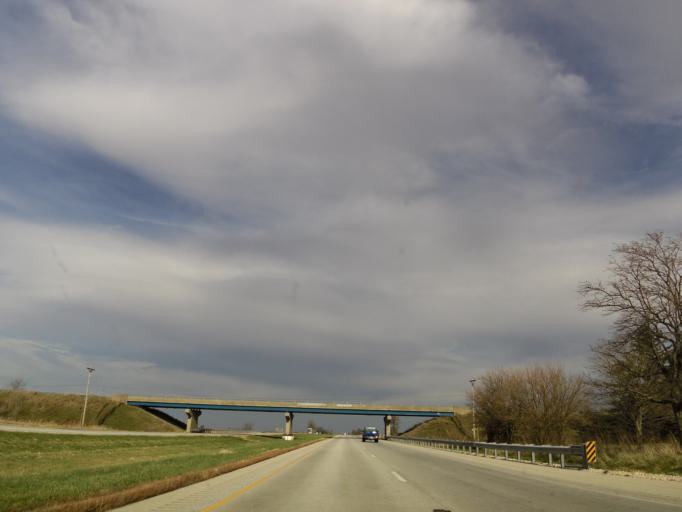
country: US
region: Illinois
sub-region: Knox County
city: Galesburg
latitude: 41.0229
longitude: -90.3345
